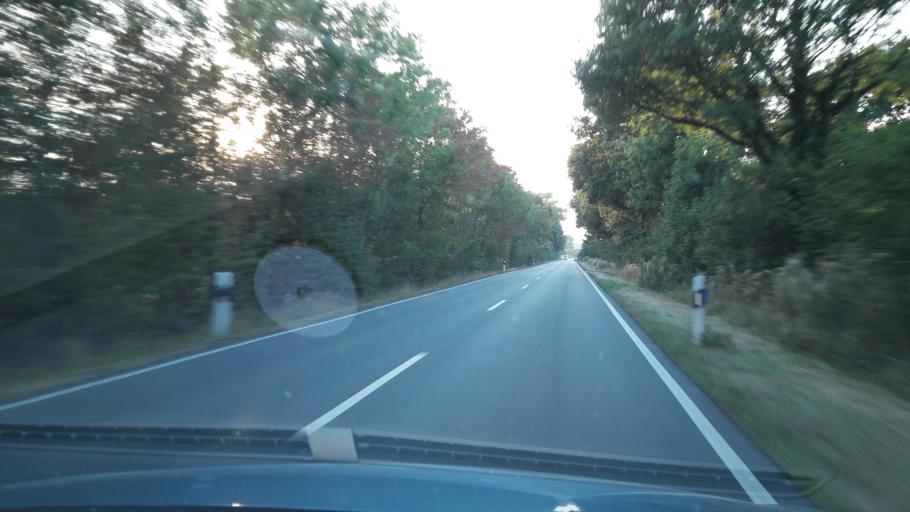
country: DE
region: North Rhine-Westphalia
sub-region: Regierungsbezirk Munster
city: Ennigerloh
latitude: 51.8118
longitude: 7.9820
